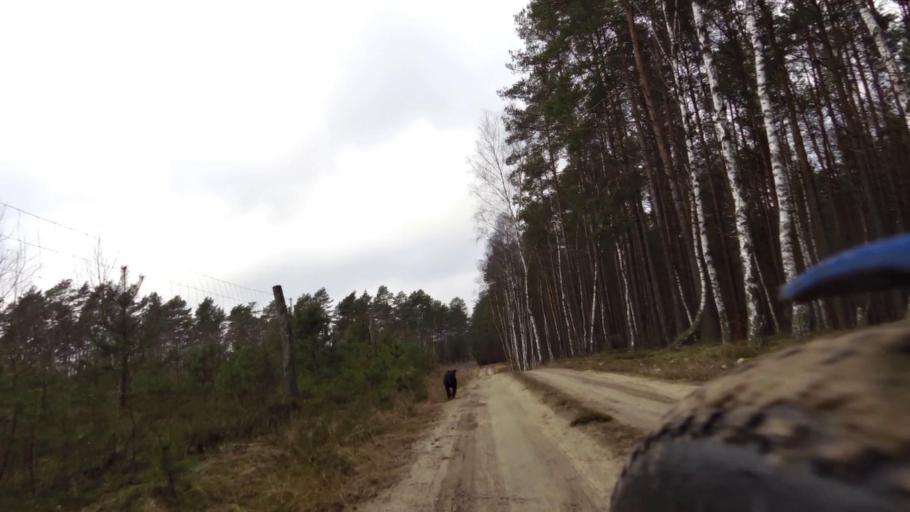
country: PL
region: West Pomeranian Voivodeship
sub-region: Powiat szczecinecki
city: Szczecinek
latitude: 53.6044
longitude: 16.6513
